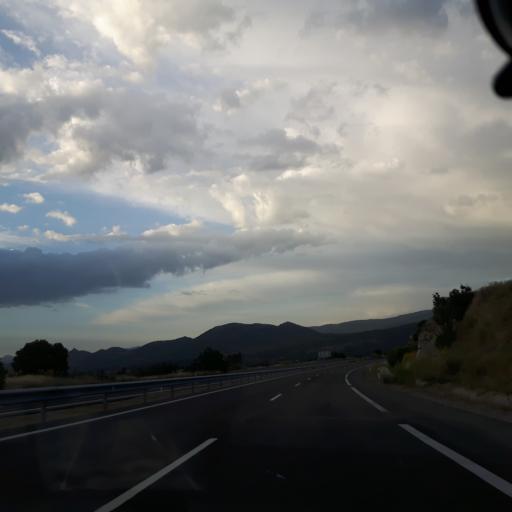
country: ES
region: Castille and Leon
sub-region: Provincia de Salamanca
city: Nava de Bejar
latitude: 40.4671
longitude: -5.6792
